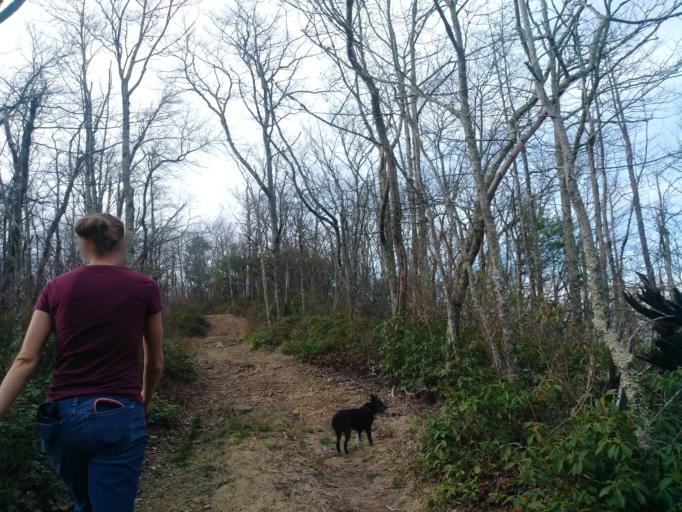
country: US
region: Tennessee
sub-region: Greene County
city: Tusculum
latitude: 36.0564
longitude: -82.6734
